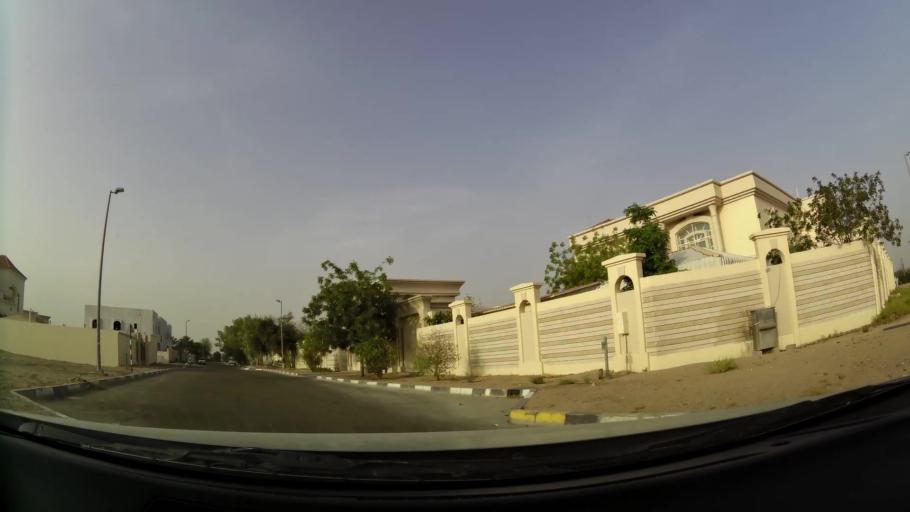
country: AE
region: Abu Dhabi
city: Al Ain
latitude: 24.1274
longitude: 55.7097
